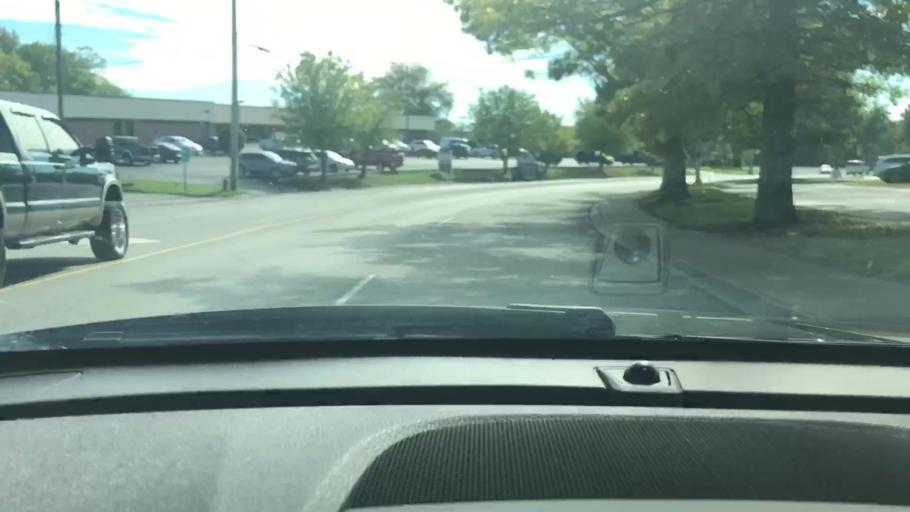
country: US
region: Tennessee
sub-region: Sumner County
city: Hendersonville
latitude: 36.3010
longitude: -86.6314
